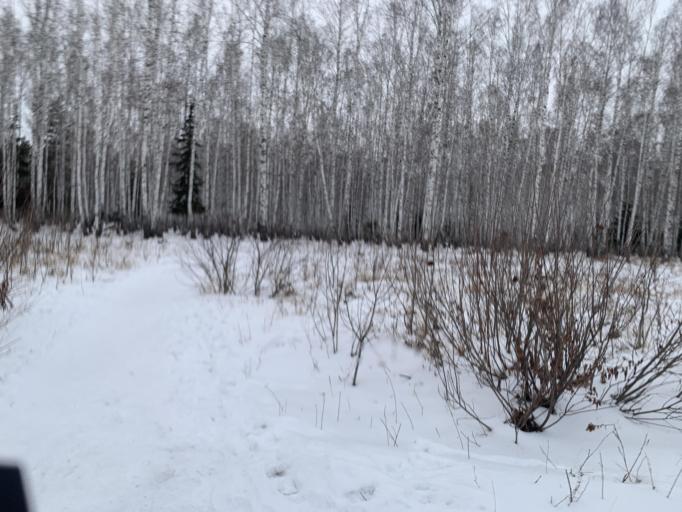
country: RU
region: Chelyabinsk
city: Roshchino
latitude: 55.2038
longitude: 61.2610
